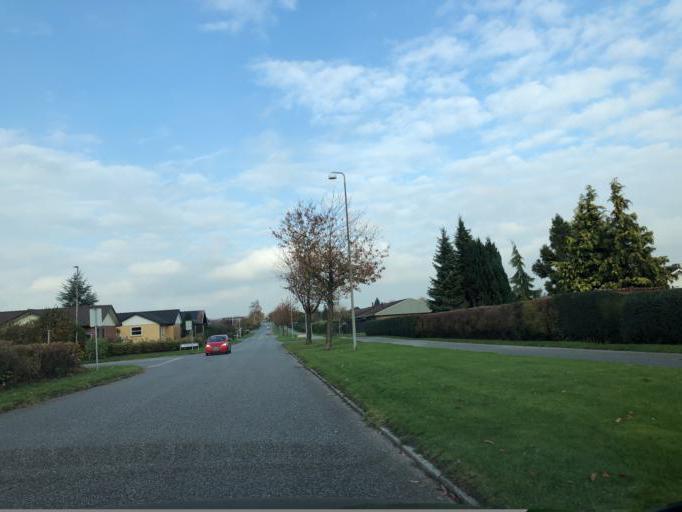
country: DK
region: South Denmark
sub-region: Vejle Kommune
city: Vejle
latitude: 55.7173
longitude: 9.6149
